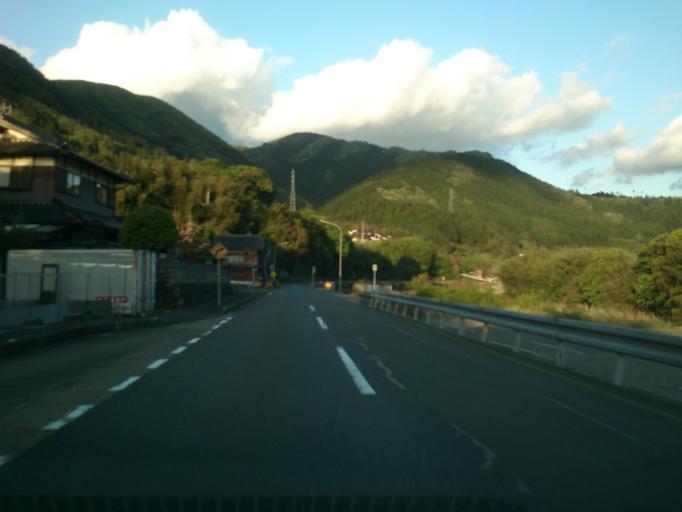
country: JP
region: Kyoto
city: Ayabe
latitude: 35.2717
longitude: 135.3928
